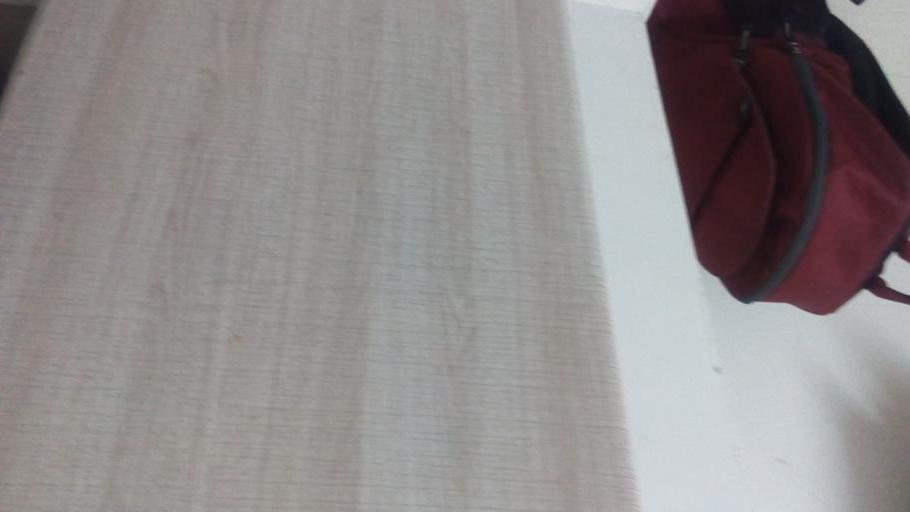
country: IN
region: Tamil Nadu
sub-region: Kancheepuram
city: Perungudi
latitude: 12.9464
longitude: 80.2336
